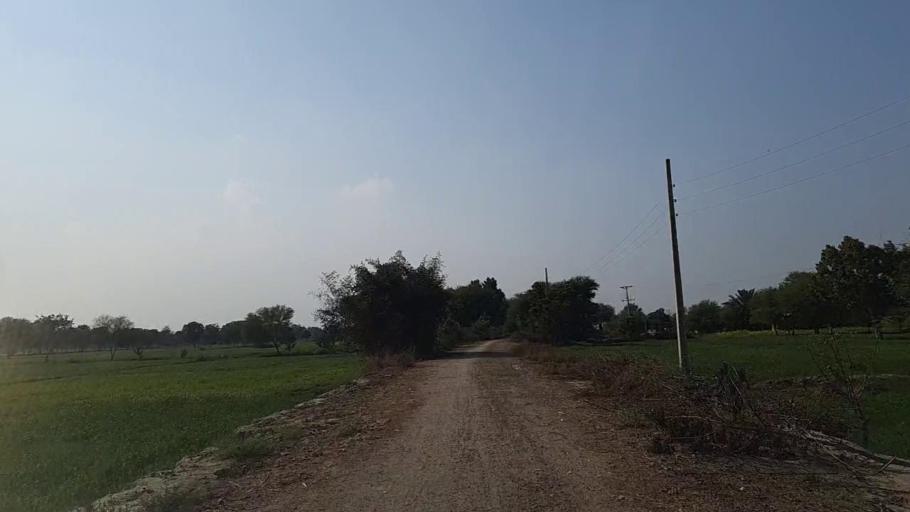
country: PK
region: Sindh
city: Jam Sahib
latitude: 26.2900
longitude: 68.5603
